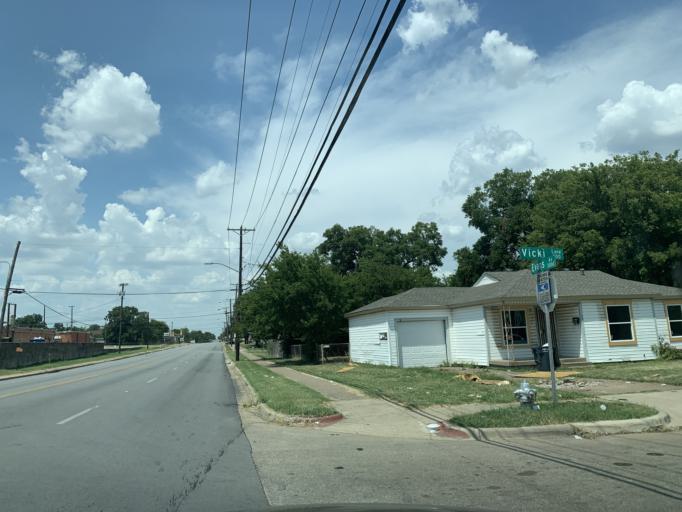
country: US
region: Texas
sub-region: Tarrant County
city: Fort Worth
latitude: 32.7070
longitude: -97.3184
